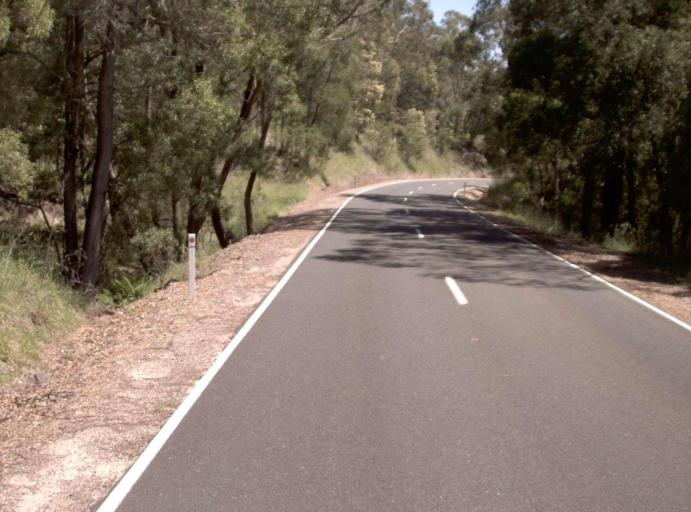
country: AU
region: Victoria
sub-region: East Gippsland
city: Lakes Entrance
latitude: -37.2420
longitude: 148.2558
